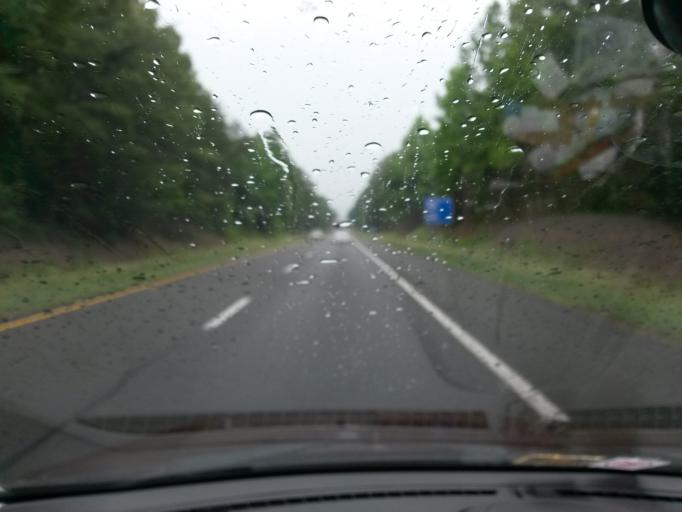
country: US
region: Virginia
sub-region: Louisa County
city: Louisa
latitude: 37.8539
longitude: -77.9932
